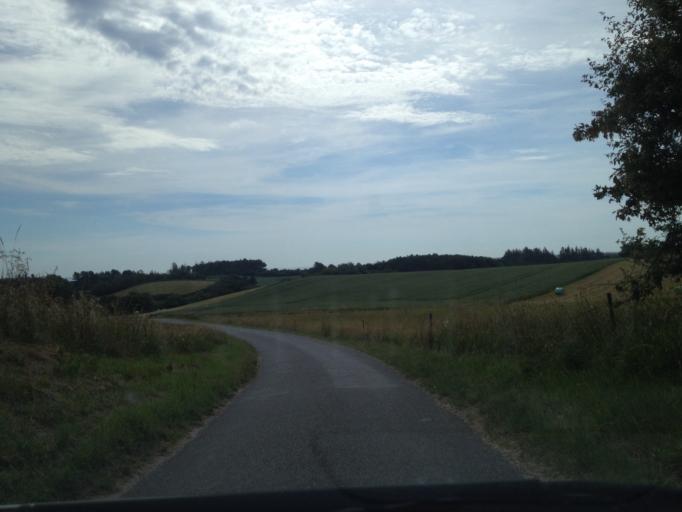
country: DK
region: Central Jutland
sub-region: Samso Kommune
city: Tranebjerg
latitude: 55.9692
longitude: 10.5312
